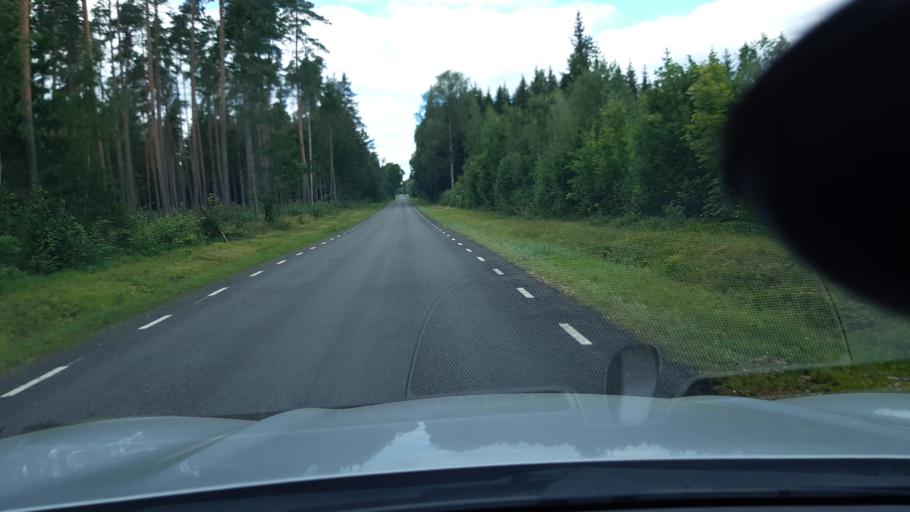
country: EE
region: Raplamaa
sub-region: Rapla vald
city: Rapla
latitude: 58.8827
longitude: 24.7344
